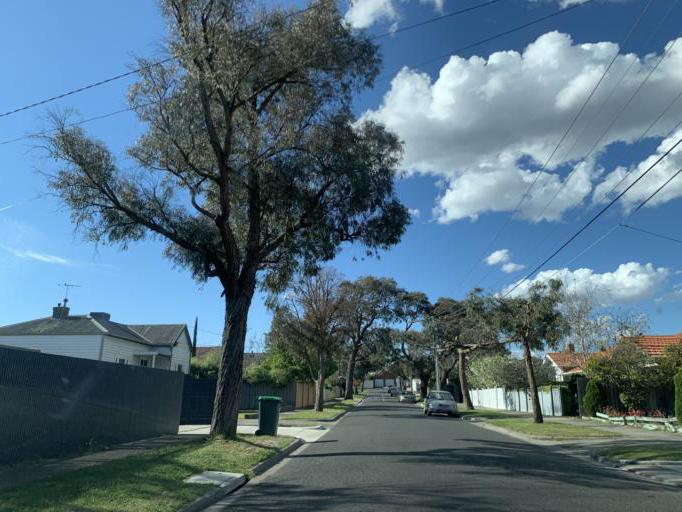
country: AU
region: Victoria
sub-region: Bayside
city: Hampton
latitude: -37.9463
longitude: 145.0109
